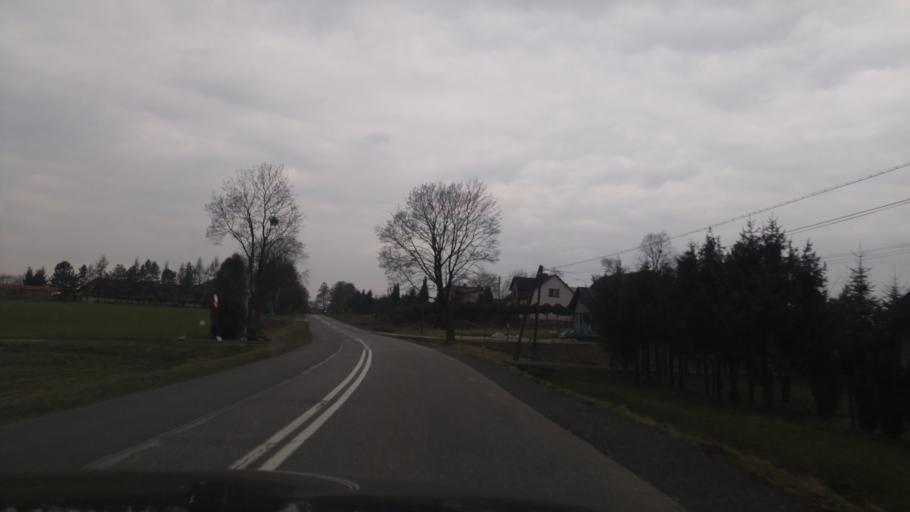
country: PL
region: Silesian Voivodeship
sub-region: Powiat cieszynski
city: Chybie
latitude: 49.9400
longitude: 18.8151
